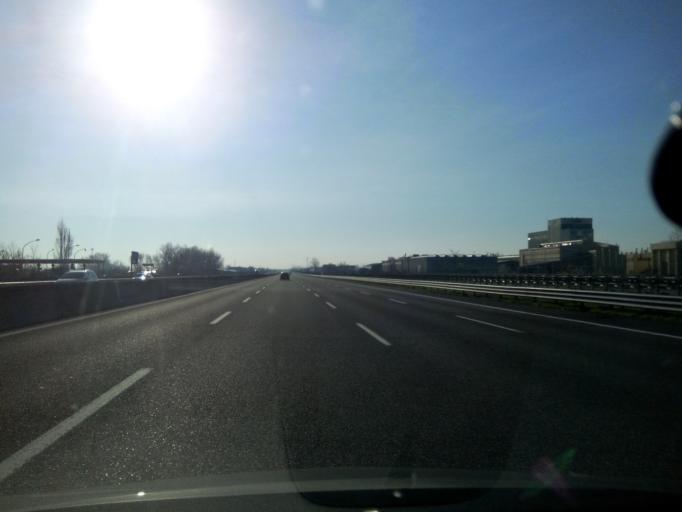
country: IT
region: Emilia-Romagna
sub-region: Provincia di Modena
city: Montale
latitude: 44.6078
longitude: 10.9095
